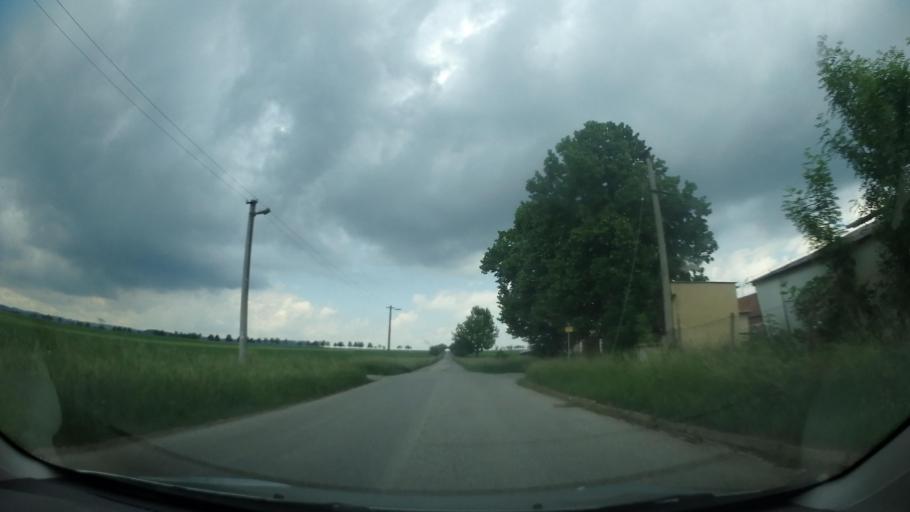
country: CZ
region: South Moravian
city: Svitavka
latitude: 49.4698
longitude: 16.6003
